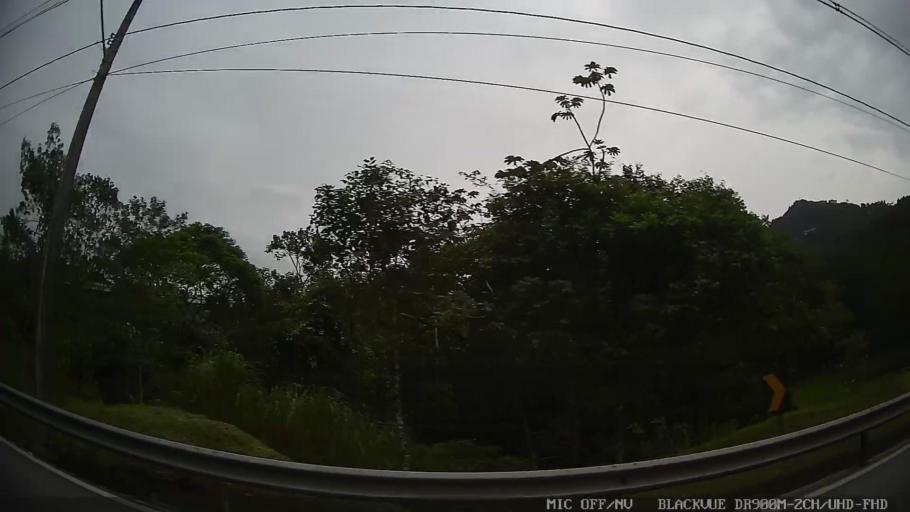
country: BR
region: Sao Paulo
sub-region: Caraguatatuba
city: Caraguatatuba
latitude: -23.6035
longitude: -45.4455
